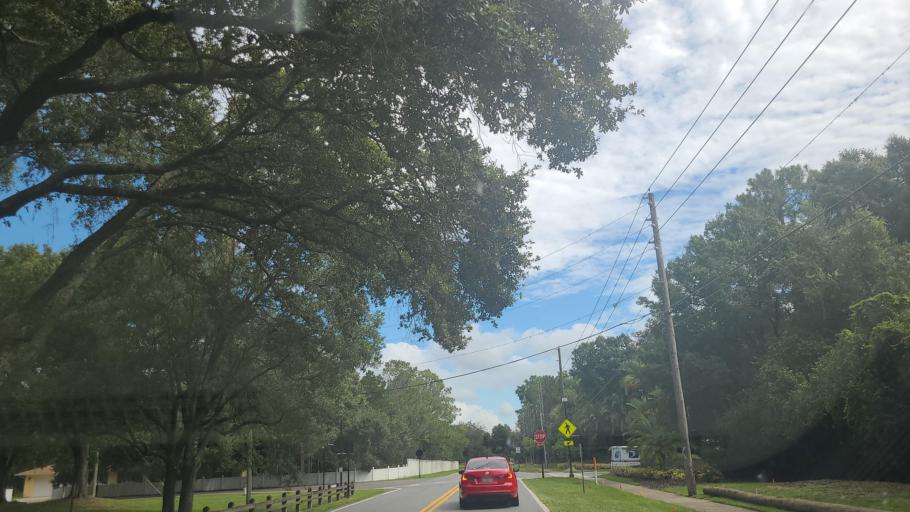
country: US
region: Florida
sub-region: Orange County
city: Lake Butler
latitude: 28.5110
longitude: -81.5429
